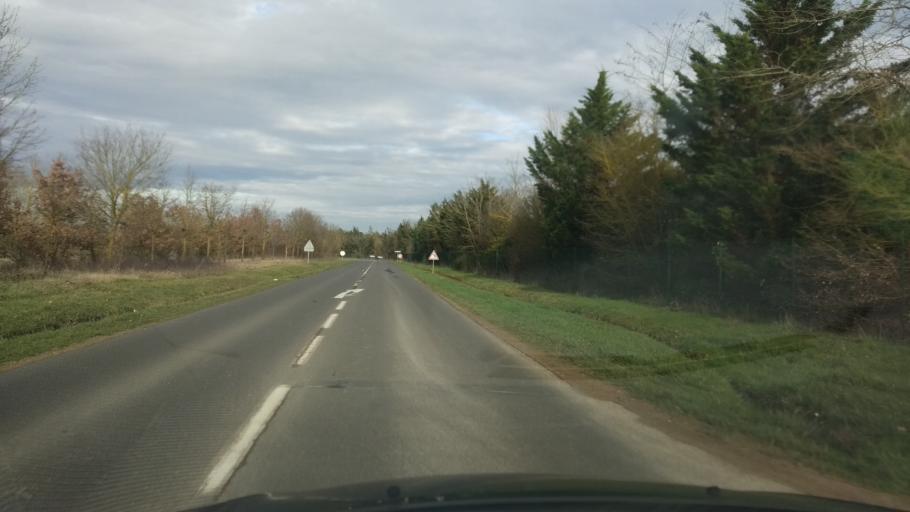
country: FR
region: Poitou-Charentes
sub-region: Departement de la Vienne
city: Saint-Georges-les-Baillargeaux
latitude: 46.6832
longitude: 0.4131
